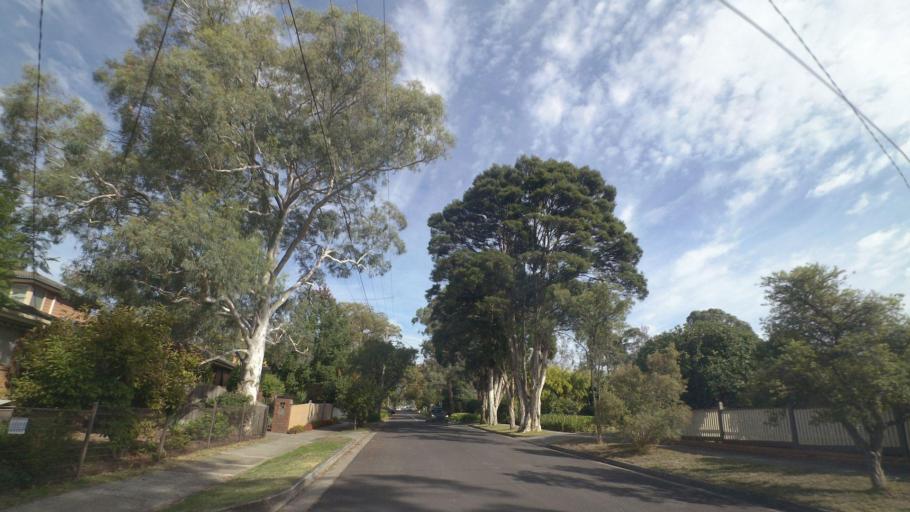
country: AU
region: Victoria
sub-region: Whitehorse
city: Blackburn
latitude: -37.8277
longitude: 145.1447
